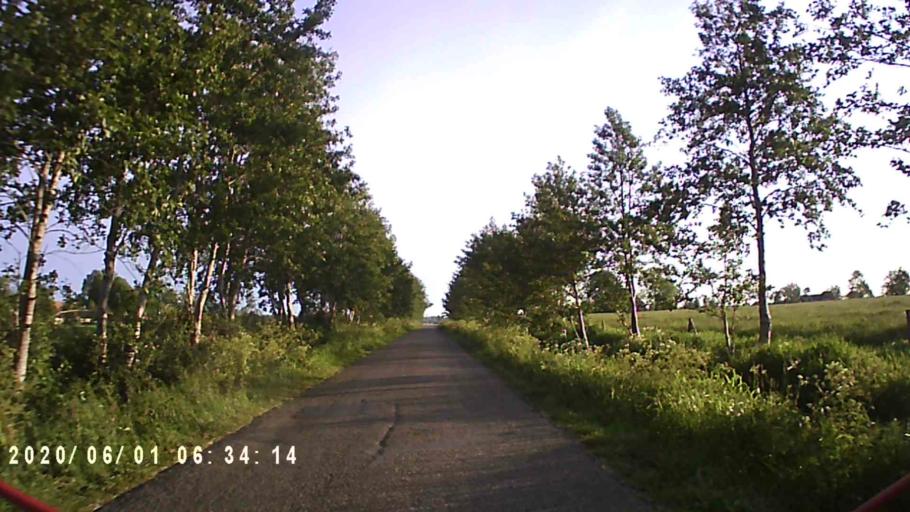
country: NL
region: Friesland
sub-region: Gemeente Kollumerland en Nieuwkruisland
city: Kollum
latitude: 53.2787
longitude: 6.1665
